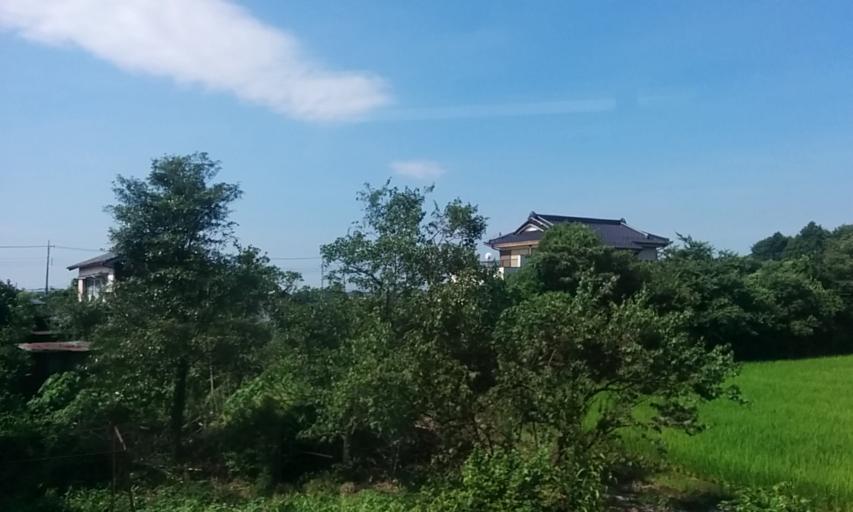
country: JP
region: Saitama
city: Hanyu
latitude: 36.1457
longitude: 139.5625
